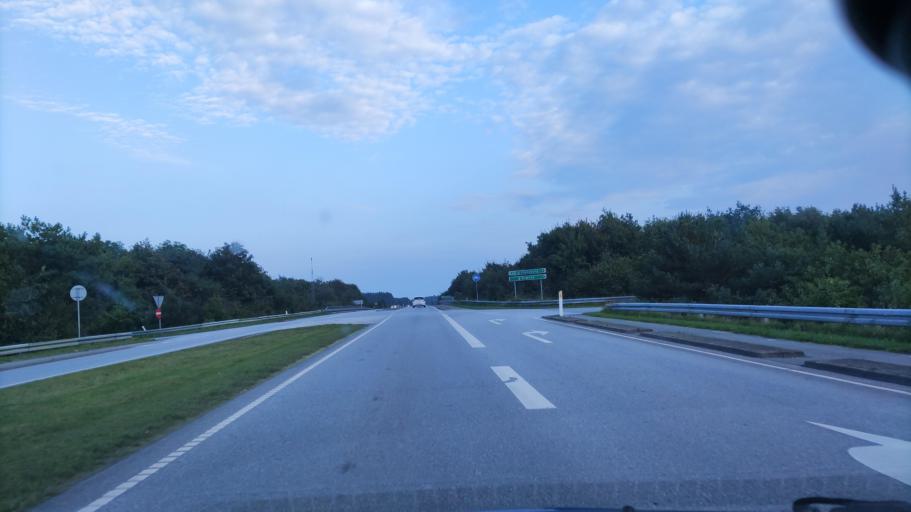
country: DK
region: South Denmark
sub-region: Aabenraa Kommune
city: Padborg
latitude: 54.8590
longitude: 9.3604
